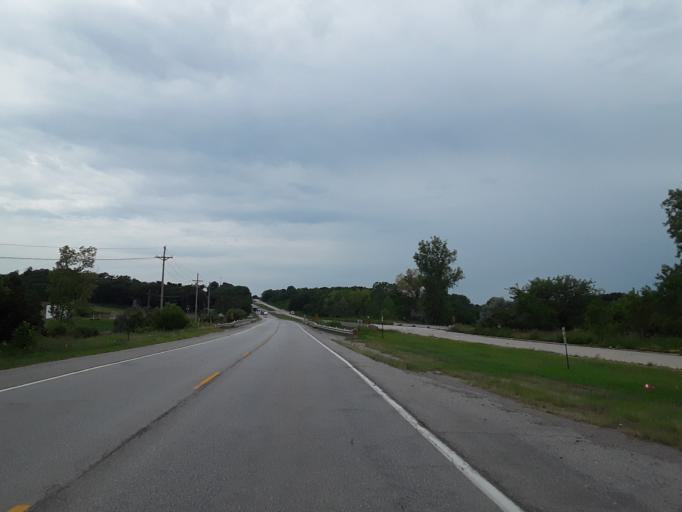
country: US
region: Nebraska
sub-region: Douglas County
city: Bennington
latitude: 41.3649
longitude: -96.0538
